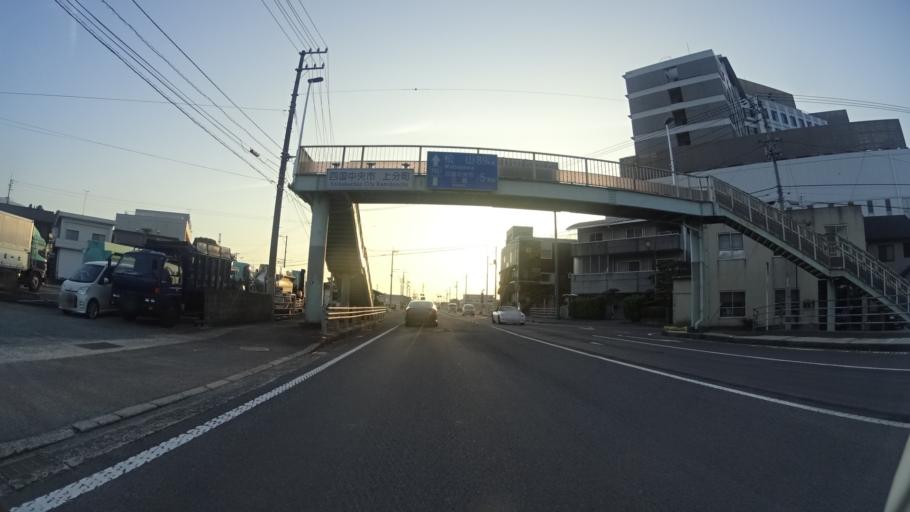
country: JP
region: Ehime
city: Kawanoecho
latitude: 33.9908
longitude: 133.5880
